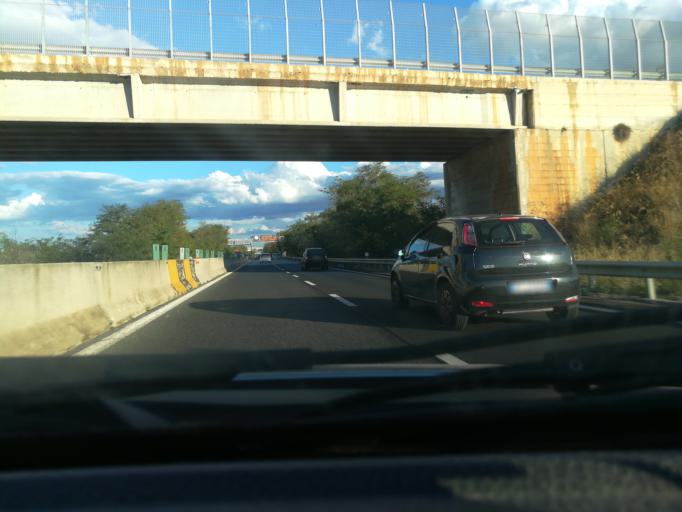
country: IT
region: Apulia
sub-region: Provincia di Bari
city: Mola di Bari
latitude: 41.0431
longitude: 17.1113
